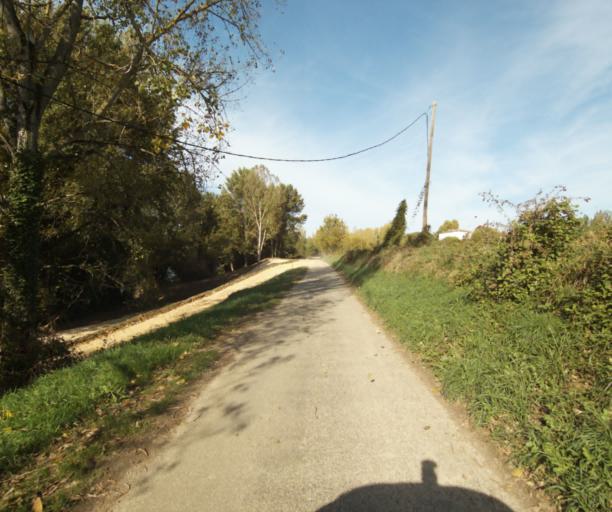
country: FR
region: Midi-Pyrenees
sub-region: Departement du Tarn-et-Garonne
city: Nohic
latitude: 43.9029
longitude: 1.4568
